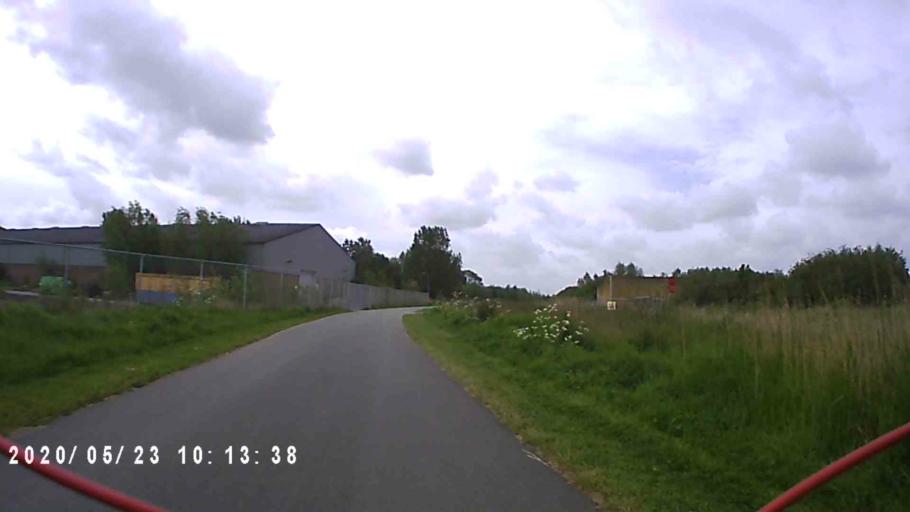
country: NL
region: Groningen
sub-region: Gemeente Appingedam
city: Appingedam
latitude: 53.3145
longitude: 6.8558
